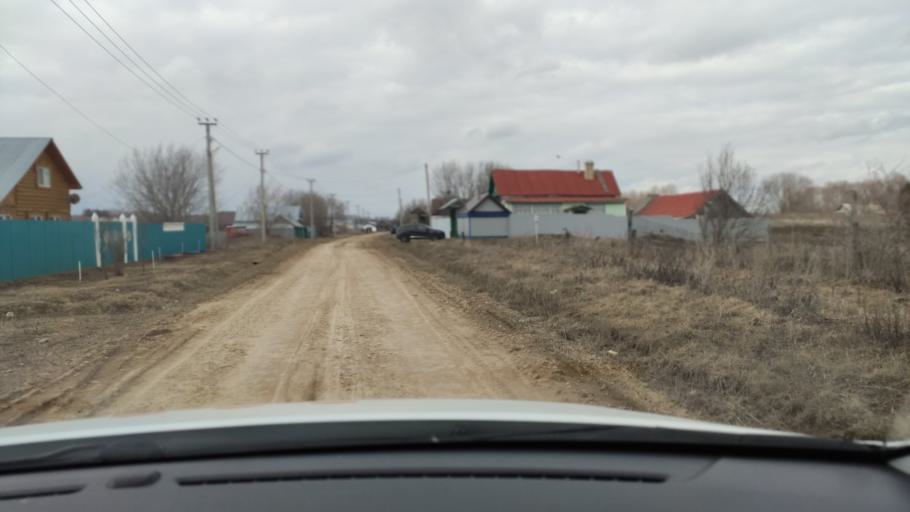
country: RU
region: Tatarstan
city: Vysokaya Gora
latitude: 56.2138
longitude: 49.3130
